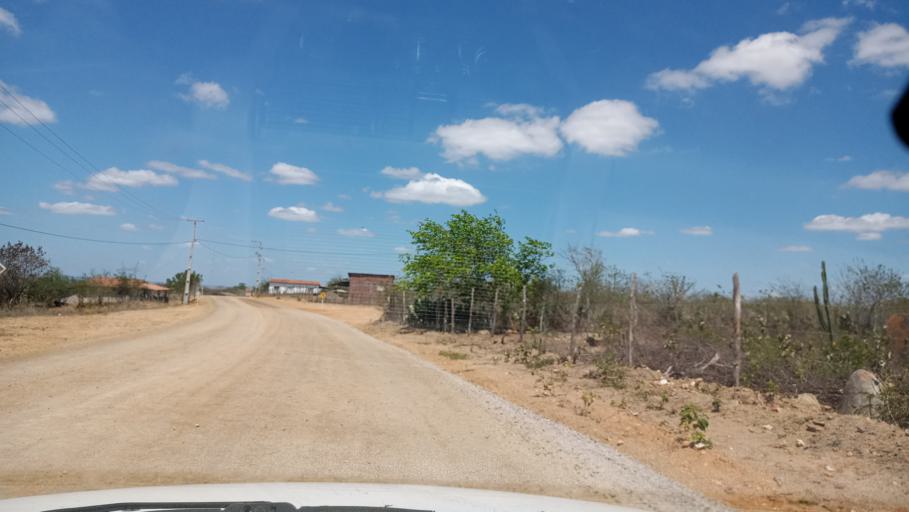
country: BR
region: Rio Grande do Norte
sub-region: Sao Paulo Do Potengi
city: Sao Paulo do Potengi
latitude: -5.7781
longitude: -35.9141
